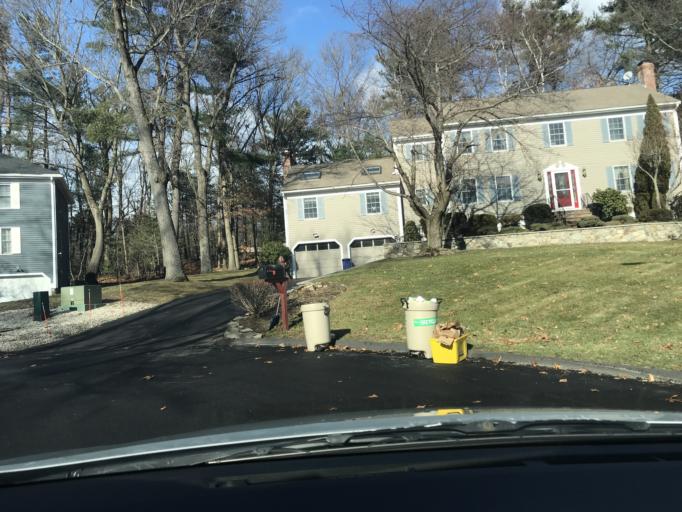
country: US
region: Massachusetts
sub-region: Middlesex County
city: Lexington
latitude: 42.4733
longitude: -71.2296
